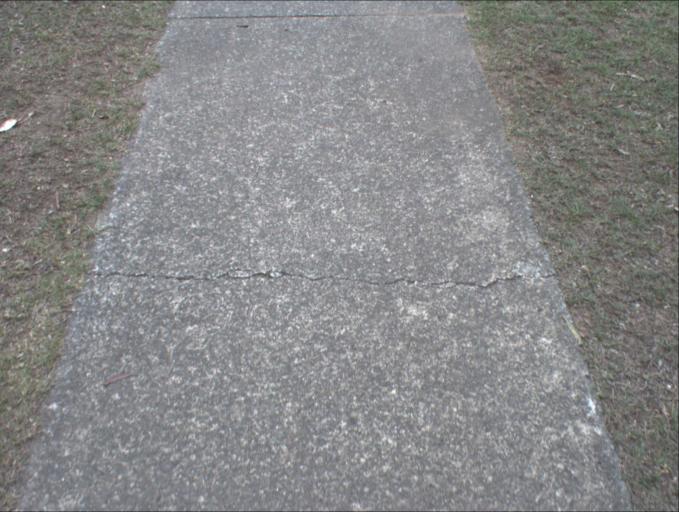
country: AU
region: Queensland
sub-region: Logan
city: Waterford West
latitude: -27.6780
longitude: 153.1341
